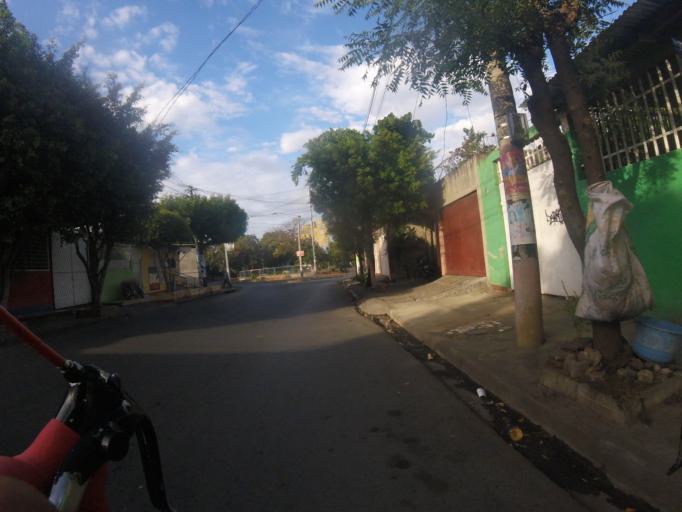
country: NI
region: Managua
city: Managua
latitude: 12.1285
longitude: -86.2272
